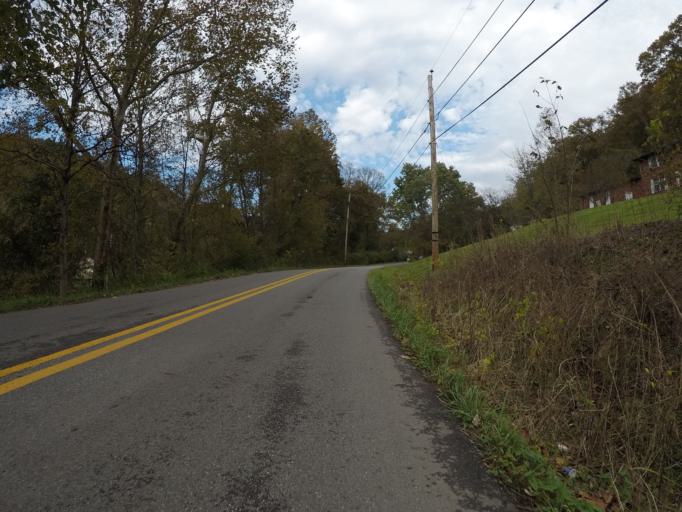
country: US
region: West Virginia
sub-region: Wayne County
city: Lavalette
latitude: 38.3409
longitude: -82.4500
